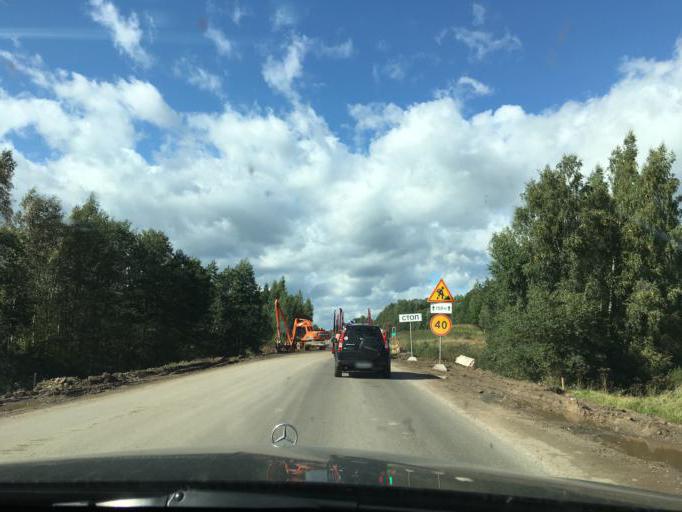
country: RU
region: Pskov
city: Novosokol'niki
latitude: 56.2799
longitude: 30.3094
